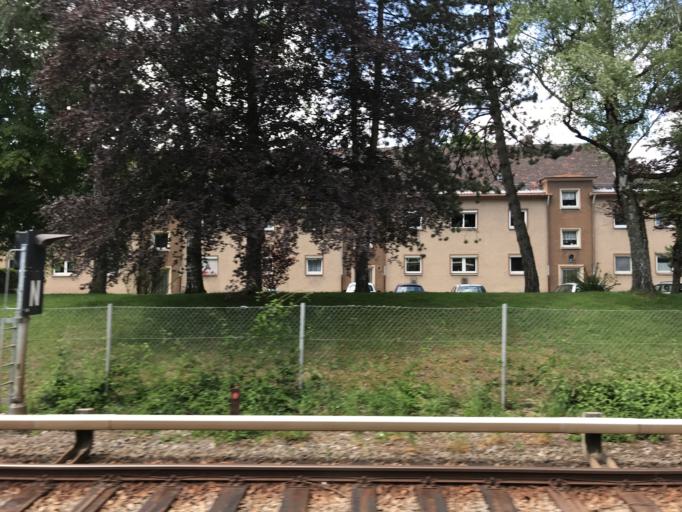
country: DE
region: Bavaria
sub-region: Upper Bavaria
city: Unterfoehring
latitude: 48.1905
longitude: 11.6136
